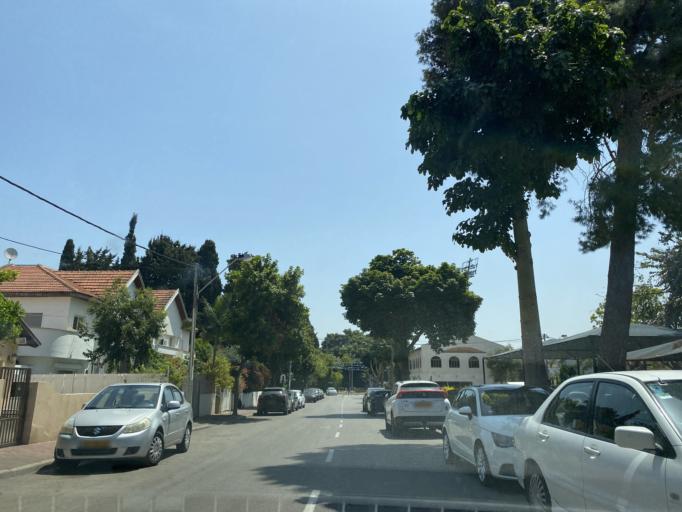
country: IL
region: Central District
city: Ra'anana
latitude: 32.1876
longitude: 34.8708
